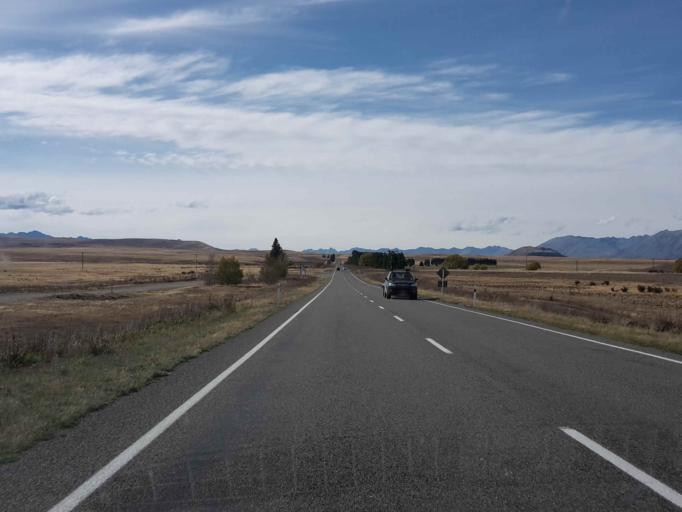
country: NZ
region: Canterbury
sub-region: Timaru District
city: Pleasant Point
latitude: -44.0671
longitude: 170.3616
